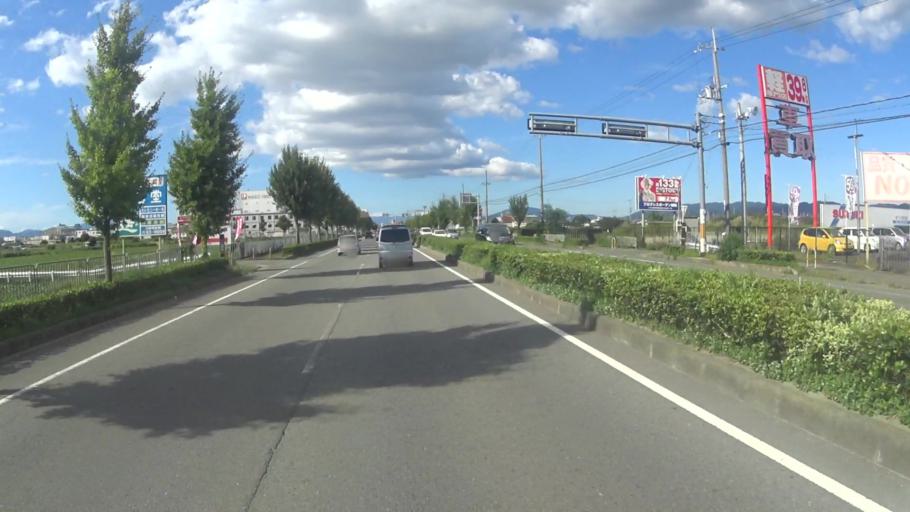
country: JP
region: Kyoto
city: Tanabe
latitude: 34.8582
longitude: 135.7622
